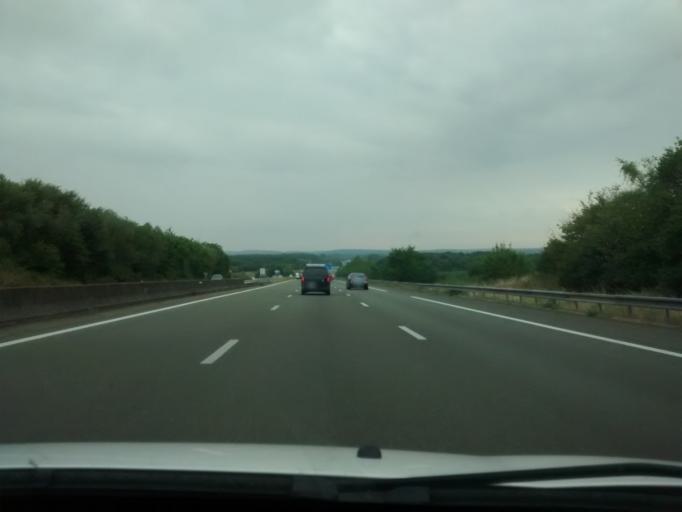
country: FR
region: Pays de la Loire
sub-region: Departement de la Sarthe
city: Sarge-les-le-Mans
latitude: 48.0495
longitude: 0.2800
